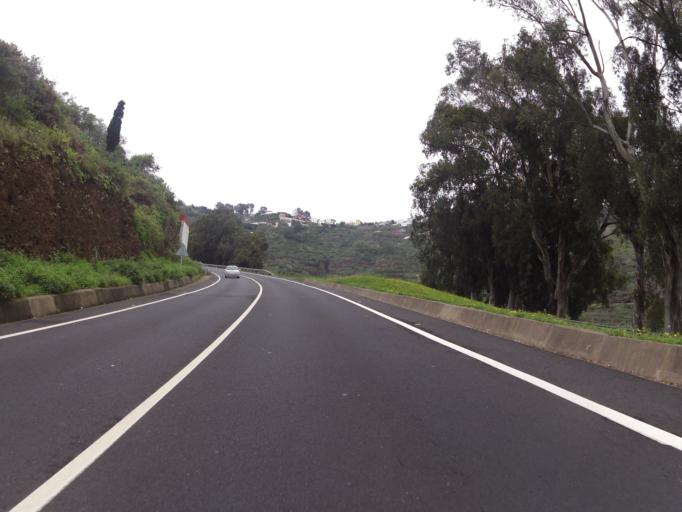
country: ES
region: Canary Islands
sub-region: Provincia de Las Palmas
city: Teror
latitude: 28.0728
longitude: -15.5299
